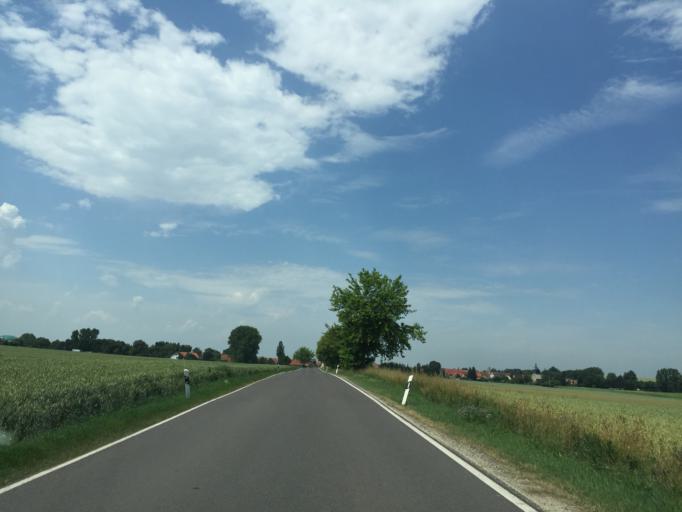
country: DE
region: Thuringia
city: Witzleben
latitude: 50.8205
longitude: 11.1225
